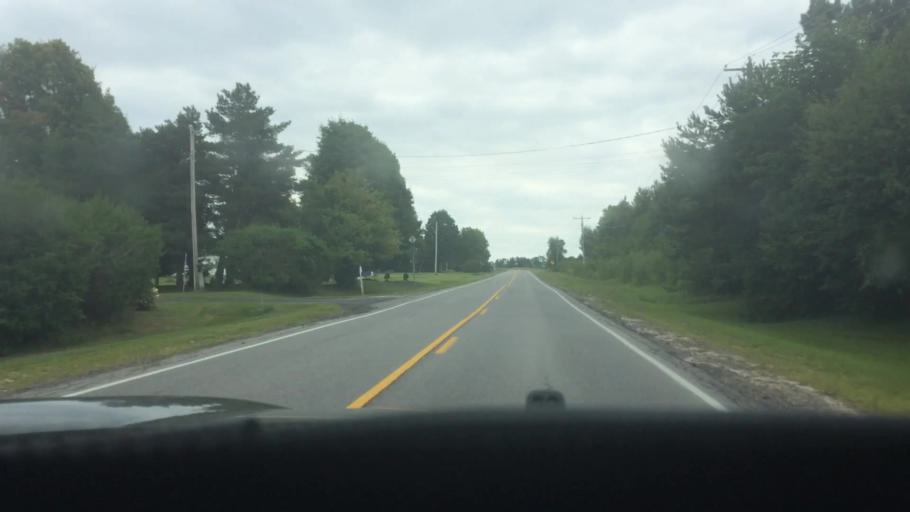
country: US
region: New York
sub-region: St. Lawrence County
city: Canton
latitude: 44.5420
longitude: -75.0948
